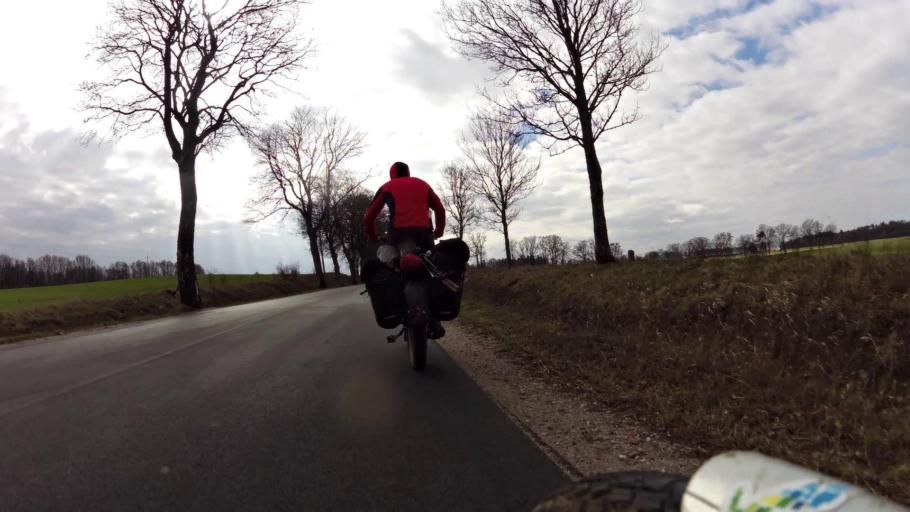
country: PL
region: Pomeranian Voivodeship
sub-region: Powiat bytowski
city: Kolczyglowy
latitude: 54.2259
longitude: 17.2416
